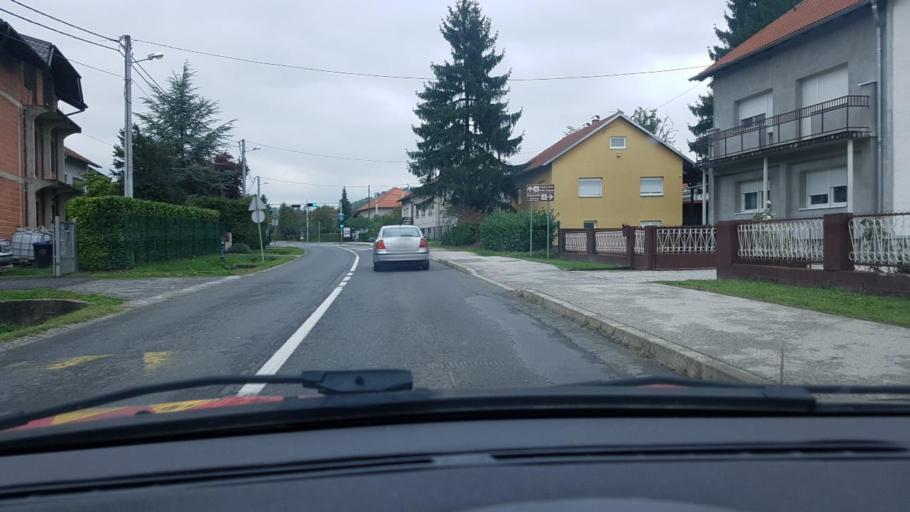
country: HR
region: Grad Zagreb
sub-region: Sesvete
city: Sesvete
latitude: 45.8766
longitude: 16.1149
